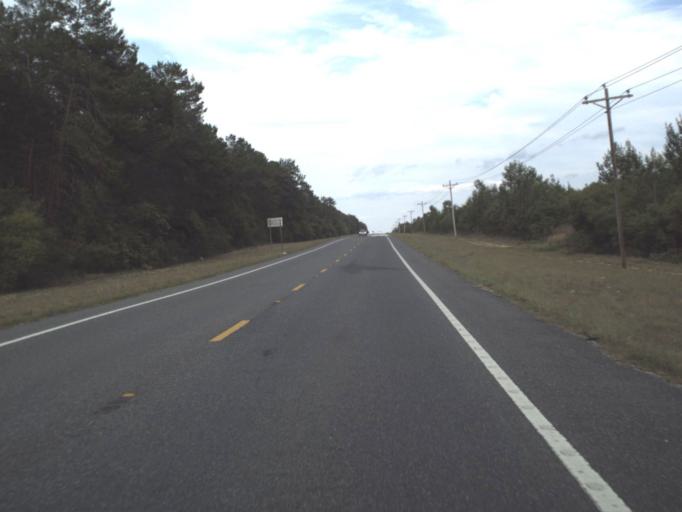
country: US
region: Florida
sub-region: Lake County
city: Astor
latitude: 29.1776
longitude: -81.7509
